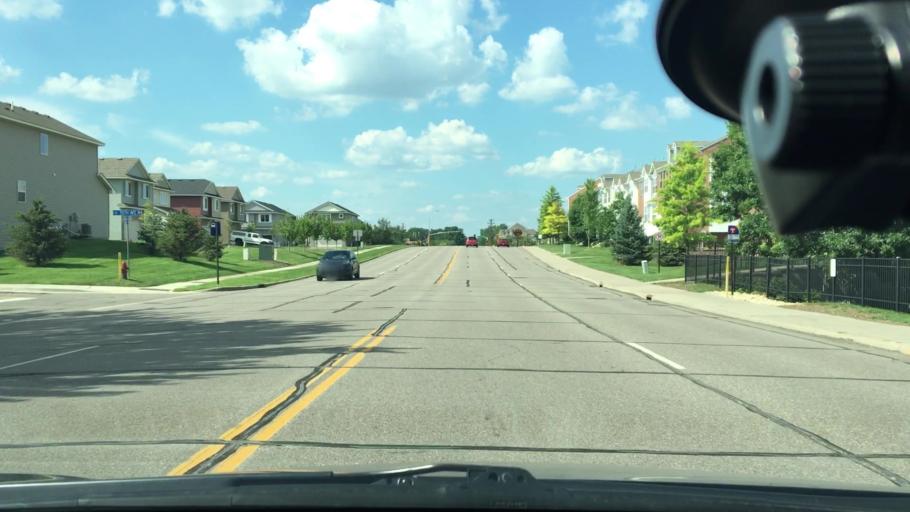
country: US
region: Minnesota
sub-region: Hennepin County
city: New Hope
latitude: 45.0527
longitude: -93.3805
